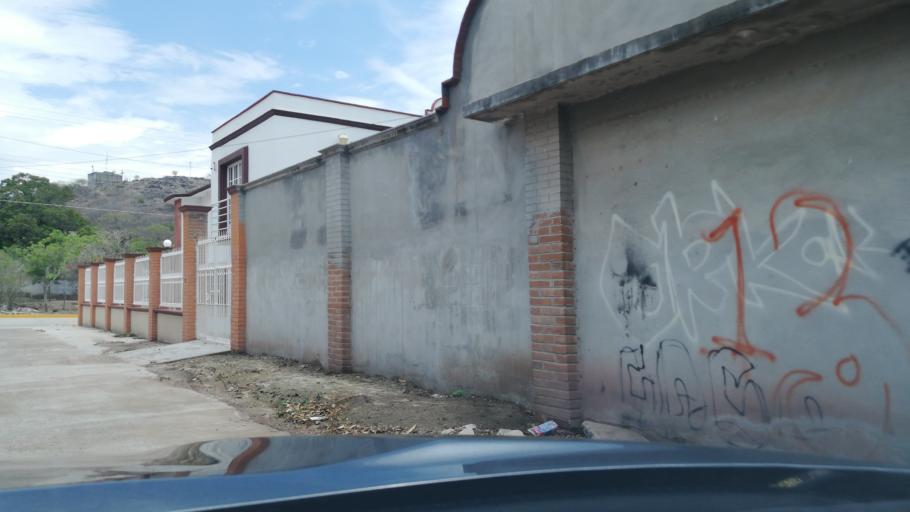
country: MX
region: Oaxaca
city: Santa Maria Jalapa del Marques
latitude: 16.4441
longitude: -95.4424
